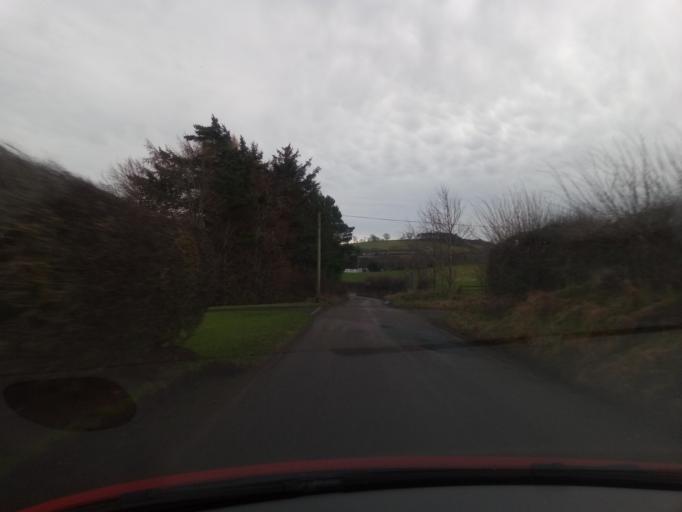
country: GB
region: England
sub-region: Northumberland
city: Wooler
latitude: 55.5507
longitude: -2.0283
